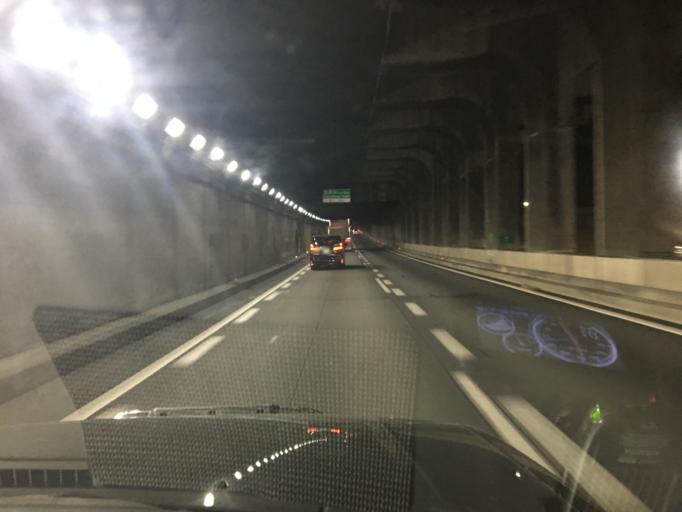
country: JP
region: Aichi
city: Kasugai
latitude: 35.2136
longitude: 136.9780
